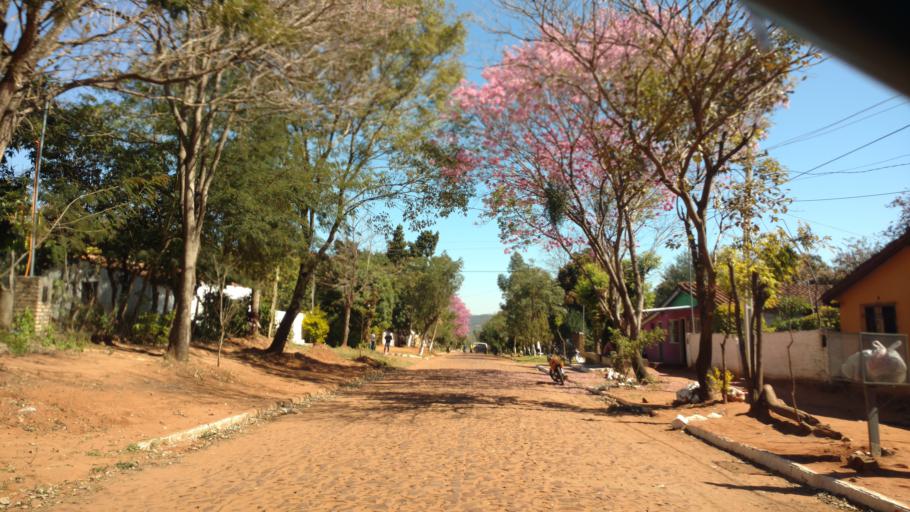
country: PY
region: Paraguari
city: Yaguaron
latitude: -25.5635
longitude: -57.2965
